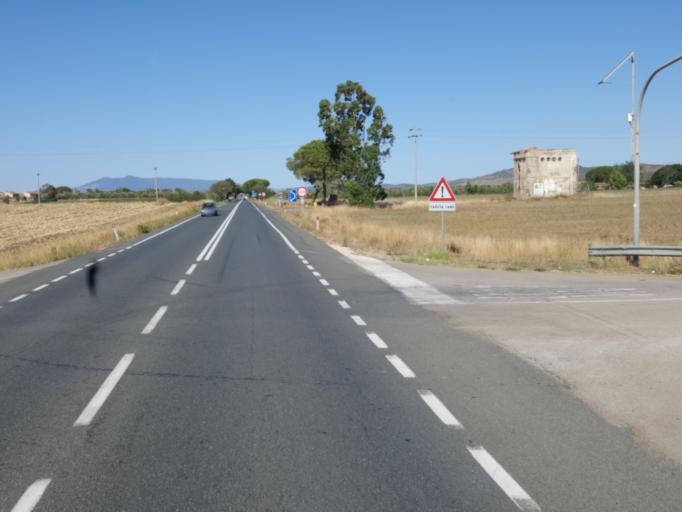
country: IT
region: Tuscany
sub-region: Provincia di Grosseto
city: Capalbio
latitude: 42.4146
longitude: 11.4234
